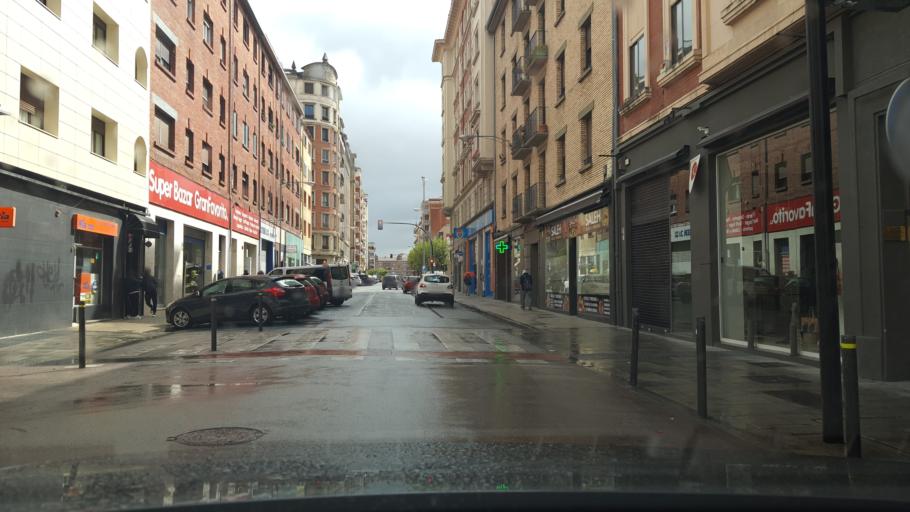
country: ES
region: Navarre
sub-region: Provincia de Navarra
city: Segundo Ensanche
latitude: 42.8103
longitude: -1.6388
